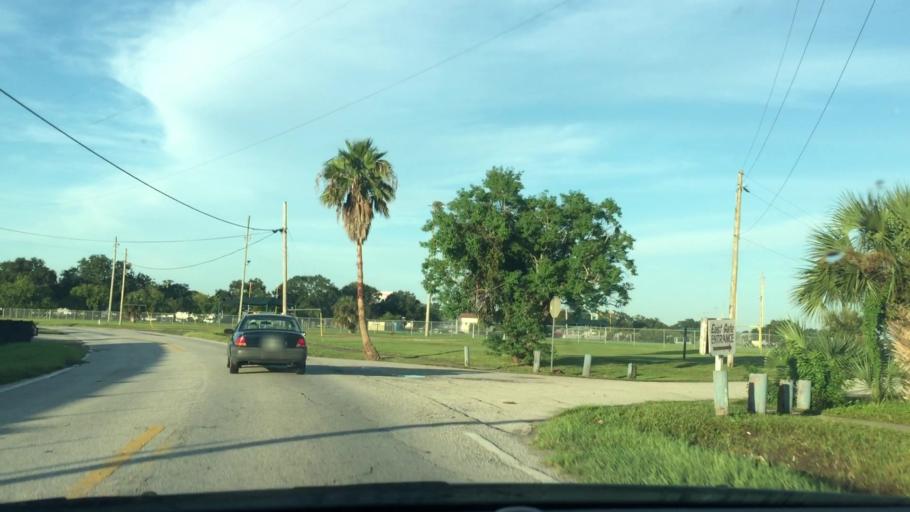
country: US
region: Florida
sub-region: Orange County
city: Pine Hills
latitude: 28.5547
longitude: -81.4321
